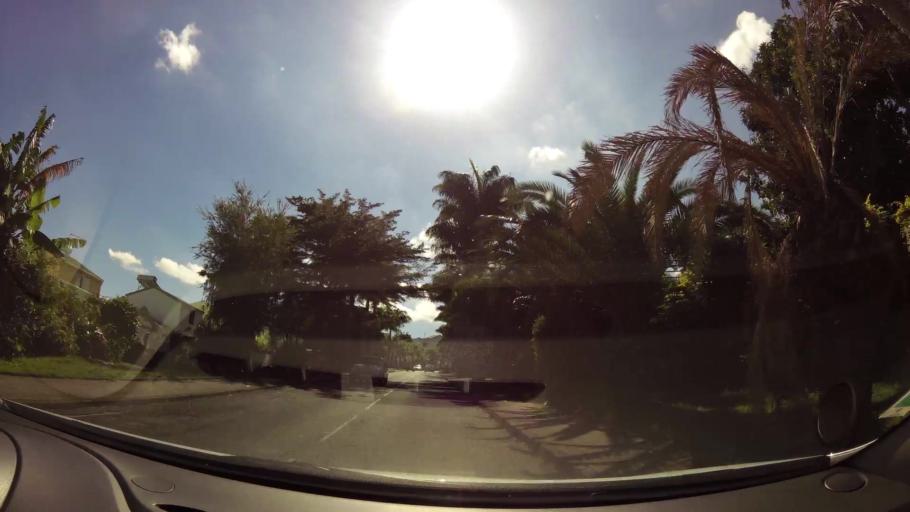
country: RE
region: Reunion
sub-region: Reunion
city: Le Tampon
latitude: -21.2789
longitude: 55.5024
